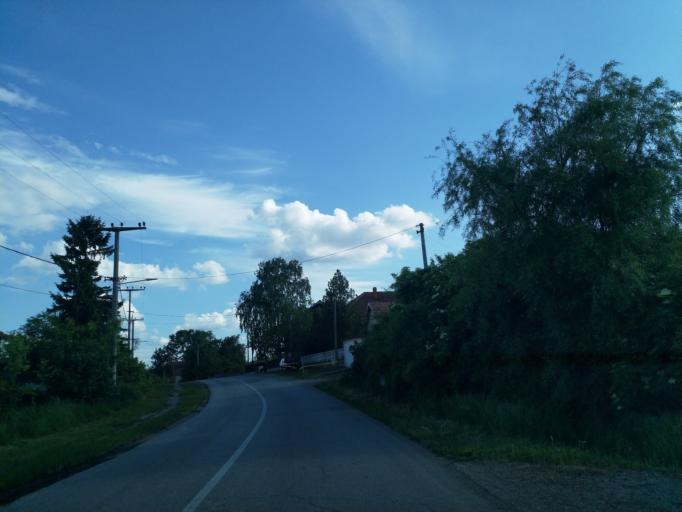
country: RS
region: Central Serbia
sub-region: Sumadijski Okrug
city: Lapovo
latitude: 44.1752
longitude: 21.0905
